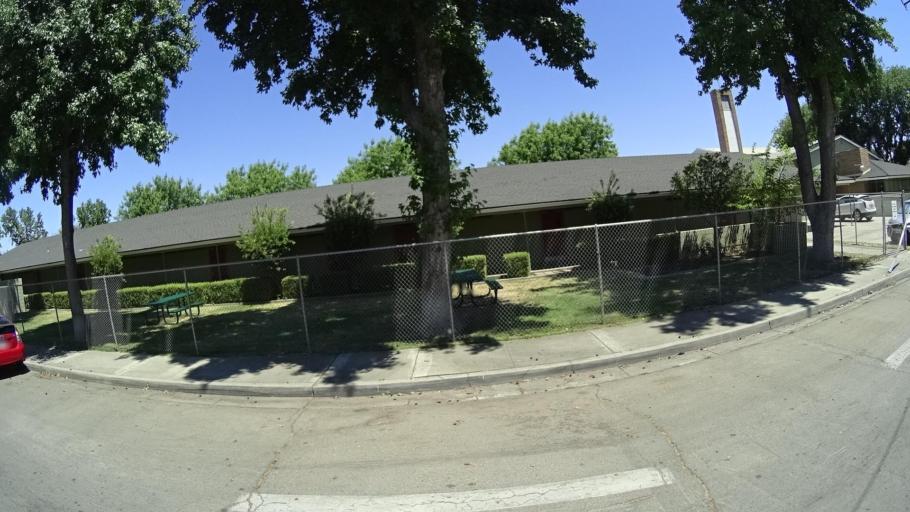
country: US
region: California
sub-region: Fresno County
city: Fresno
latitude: 36.7876
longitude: -119.7940
